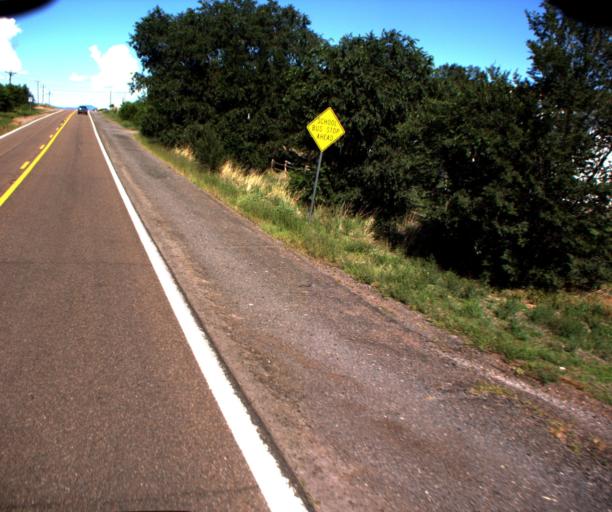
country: US
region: Arizona
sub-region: Apache County
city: Eagar
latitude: 34.1110
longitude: -109.2793
